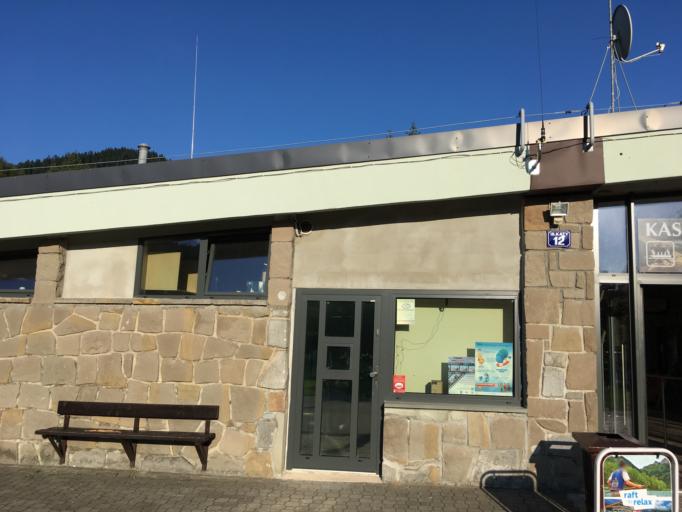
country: PL
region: Lesser Poland Voivodeship
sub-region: Powiat nowotarski
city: Krosnica
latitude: 49.4064
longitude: 20.3684
